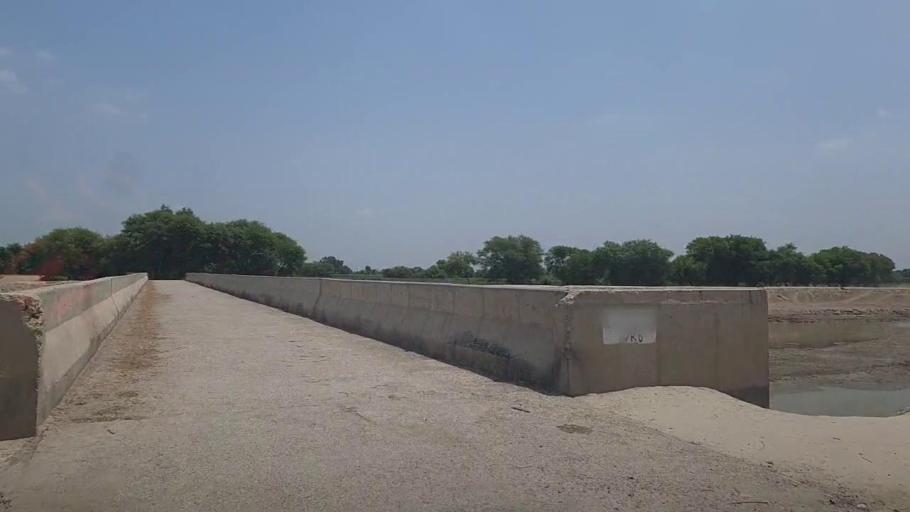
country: PK
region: Sindh
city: Ubauro
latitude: 28.2426
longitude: 69.8289
